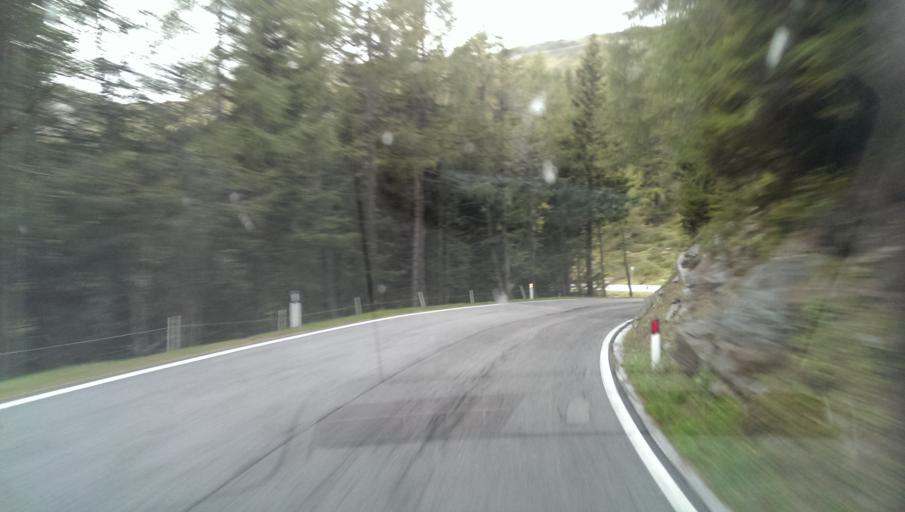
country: IT
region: Trentino-Alto Adige
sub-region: Bolzano
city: Racines
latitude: 46.8331
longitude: 11.3126
